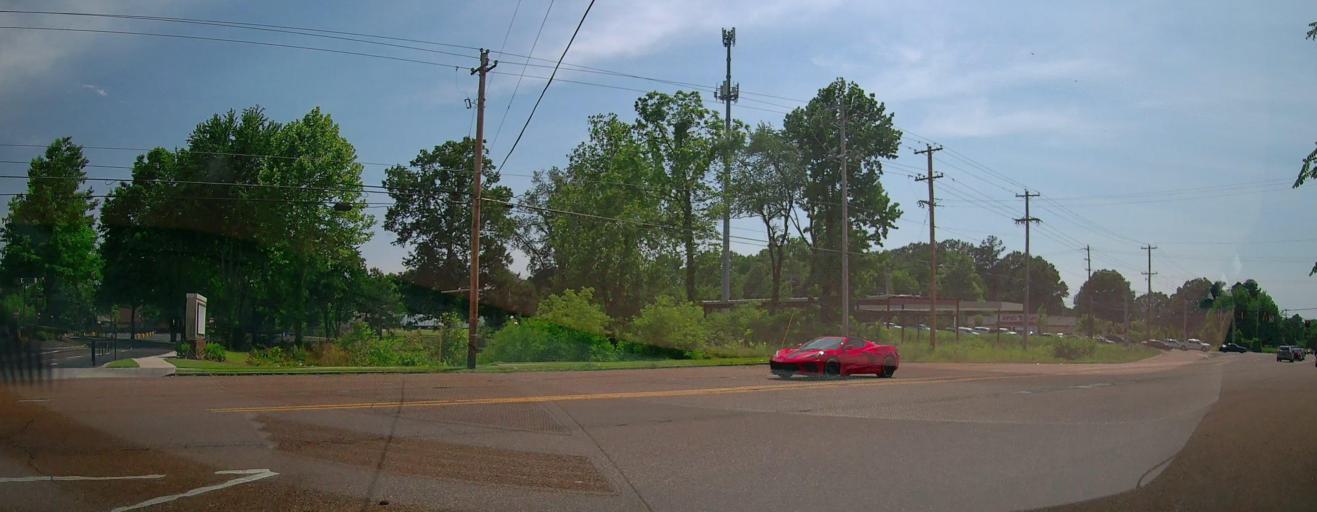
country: US
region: Mississippi
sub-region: De Soto County
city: Olive Branch
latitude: 35.0061
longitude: -89.8295
